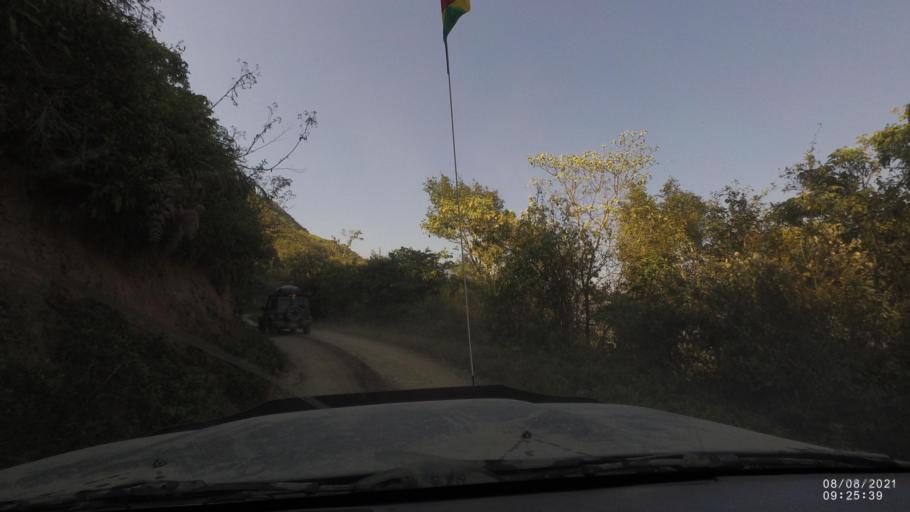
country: BO
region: La Paz
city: Quime
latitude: -16.5830
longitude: -66.7217
